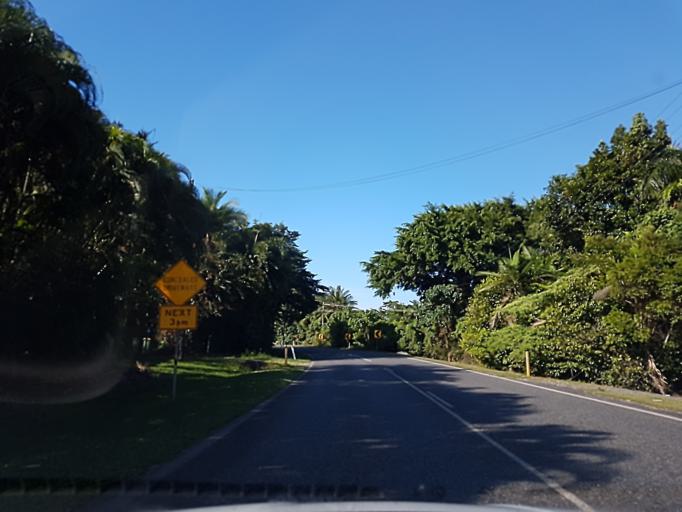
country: AU
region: Queensland
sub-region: Cairns
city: Port Douglas
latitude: -16.3902
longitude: 145.4166
